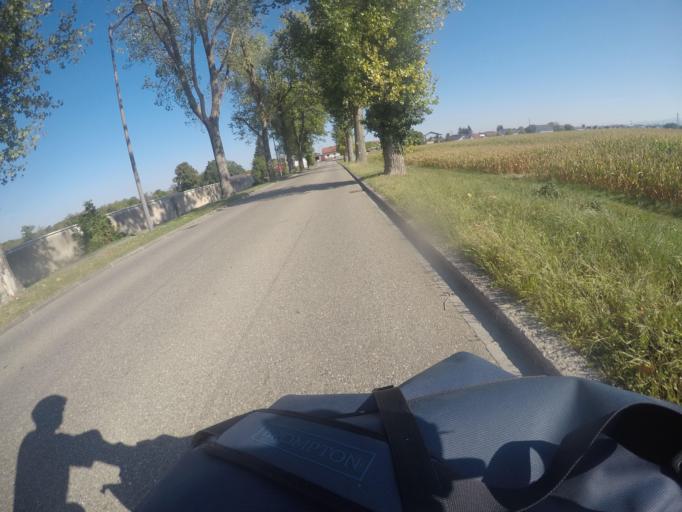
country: FR
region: Alsace
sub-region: Departement du Haut-Rhin
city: Ottmarsheim
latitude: 47.7533
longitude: 7.5048
